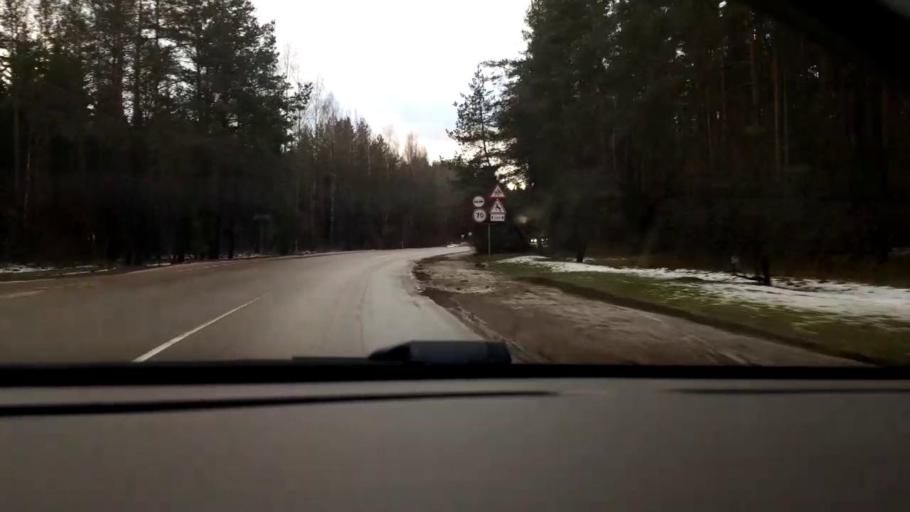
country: LT
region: Vilnius County
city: Rasos
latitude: 54.7749
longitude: 25.3840
